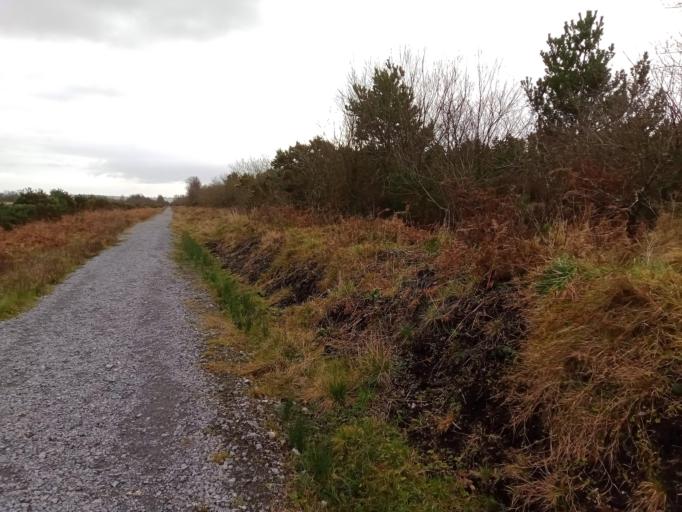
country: IE
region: Munster
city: Thurles
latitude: 52.5967
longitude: -7.7460
